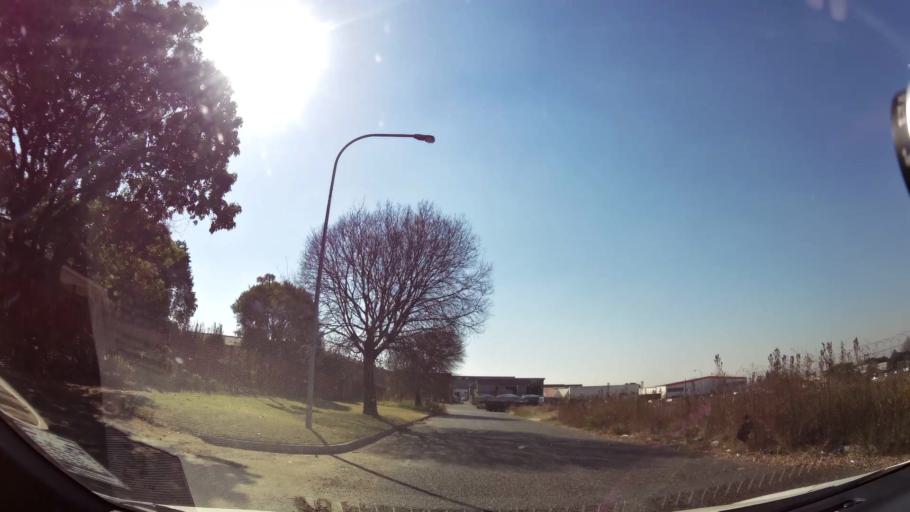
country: ZA
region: Gauteng
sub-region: City of Johannesburg Metropolitan Municipality
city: Johannesburg
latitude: -26.2500
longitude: 28.1002
